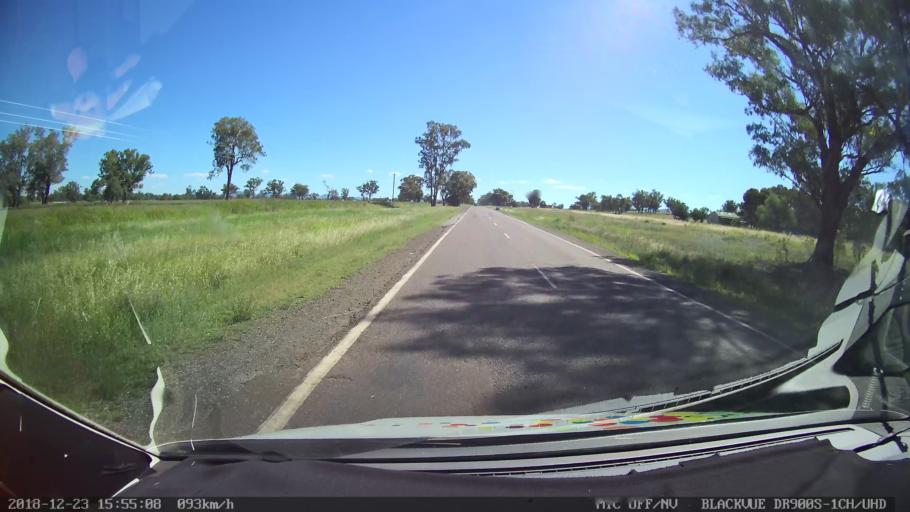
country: AU
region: New South Wales
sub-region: Tamworth Municipality
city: Phillip
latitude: -31.1523
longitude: 150.8716
